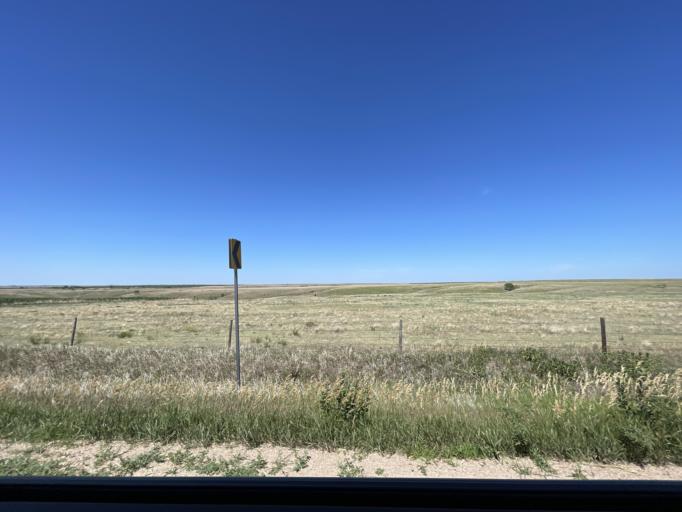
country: US
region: Nebraska
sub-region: Red Willow County
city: McCook
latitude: 40.4309
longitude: -100.7303
